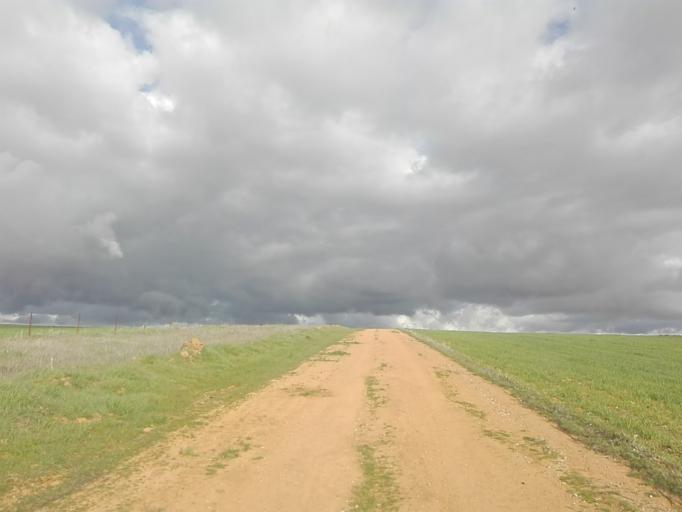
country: ES
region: Extremadura
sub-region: Provincia de Badajoz
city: Llerena
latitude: 38.2855
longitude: -6.0157
